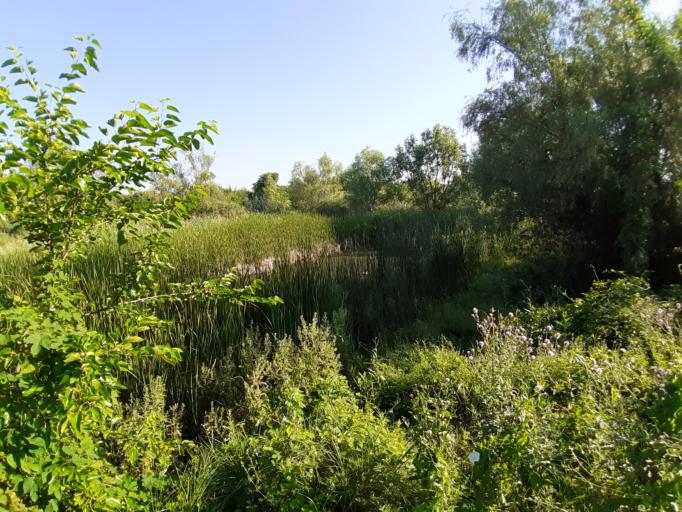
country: RO
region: Bucuresti
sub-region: Municipiul Bucuresti
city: Bucharest
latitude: 44.4036
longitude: 26.1322
